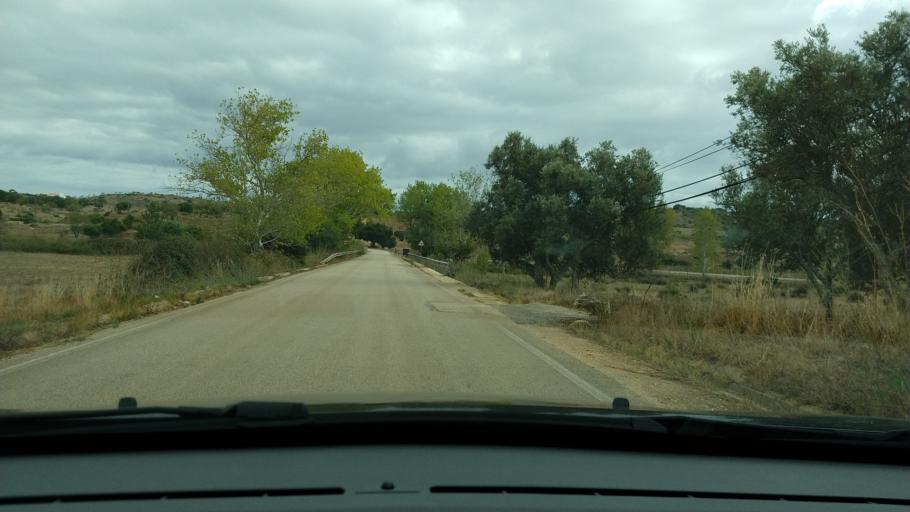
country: PT
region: Faro
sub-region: Lagos
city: Lagos
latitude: 37.0869
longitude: -8.7814
